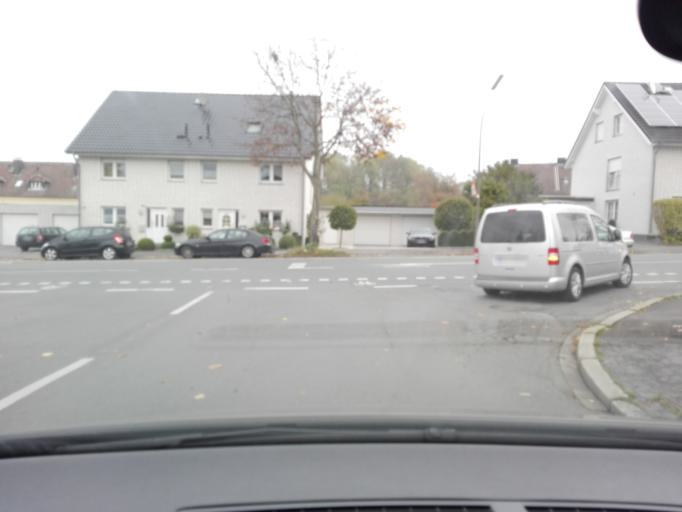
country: DE
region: North Rhine-Westphalia
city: Lanstrop
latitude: 51.5161
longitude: 7.5641
